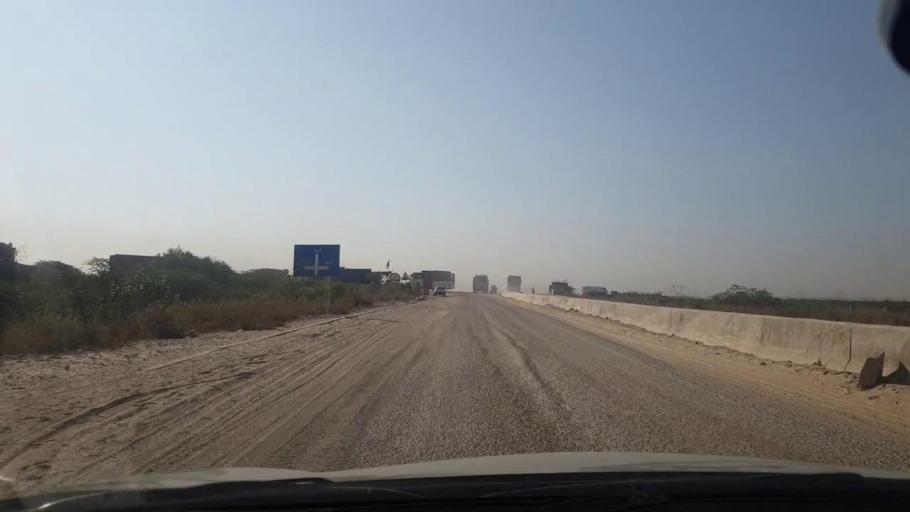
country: PK
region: Sindh
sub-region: Karachi District
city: Karachi
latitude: 25.0759
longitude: 67.0139
